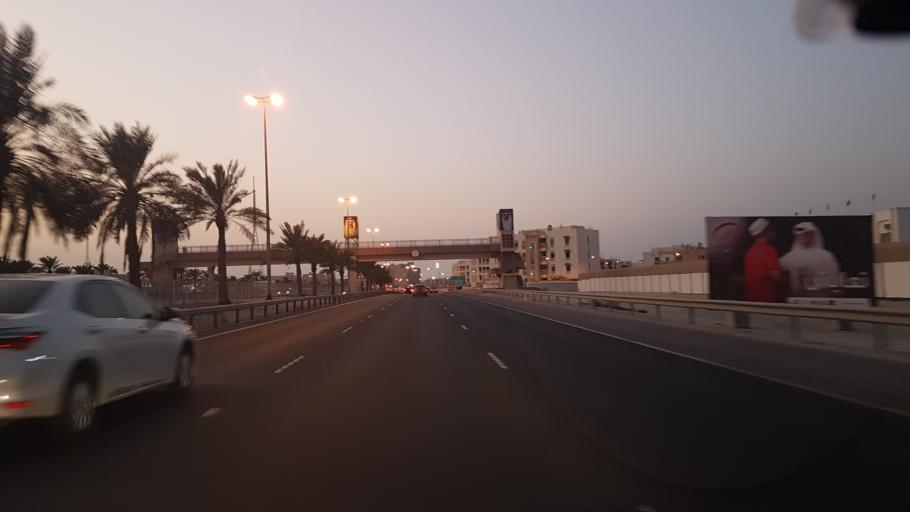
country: BH
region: Northern
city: Madinat `Isa
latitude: 26.1584
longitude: 50.5662
